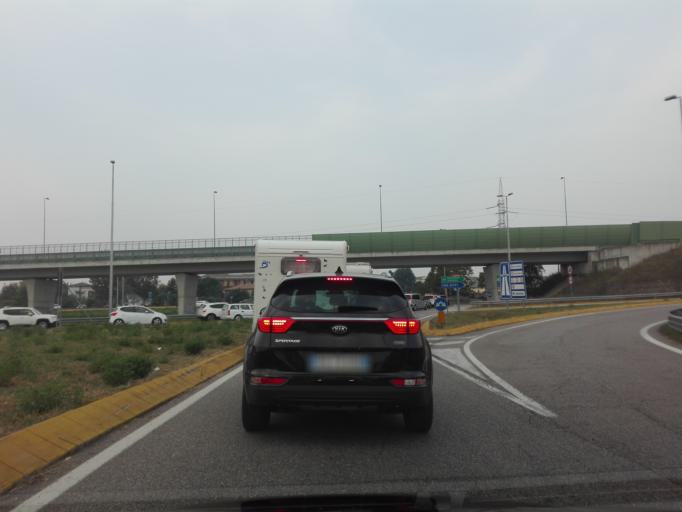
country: IT
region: Veneto
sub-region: Provincia di Verona
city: Castelnuovo del Garda
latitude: 45.4379
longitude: 10.7440
